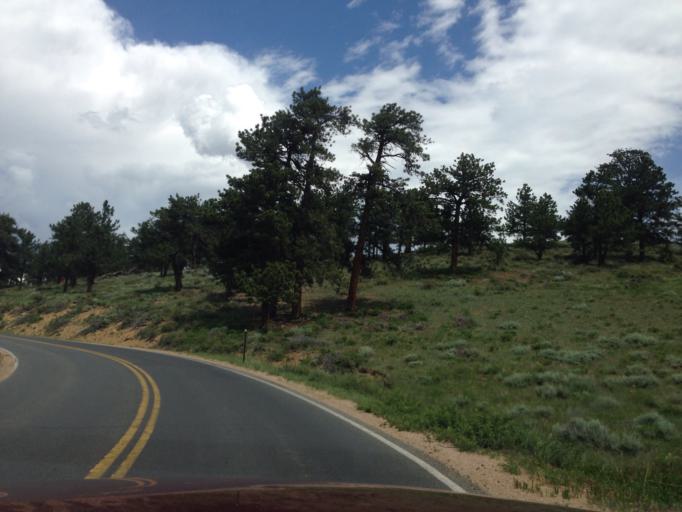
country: US
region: Colorado
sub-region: Larimer County
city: Estes Park
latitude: 40.3821
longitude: -105.6048
